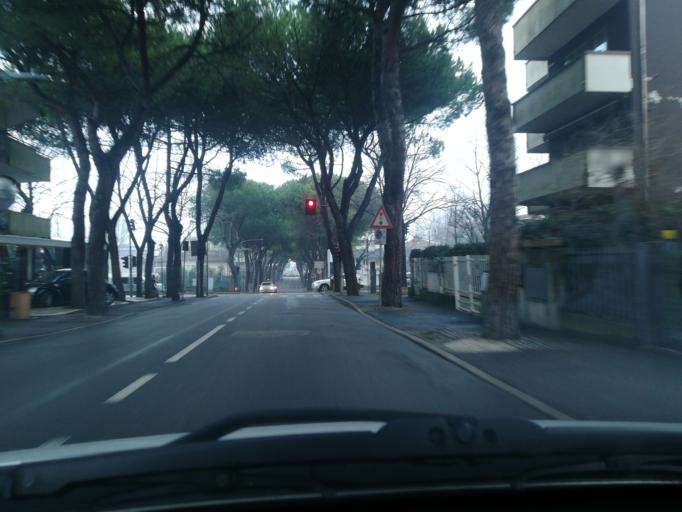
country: IT
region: Emilia-Romagna
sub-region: Provincia di Rimini
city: Riccione
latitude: 44.0048
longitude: 12.6472
